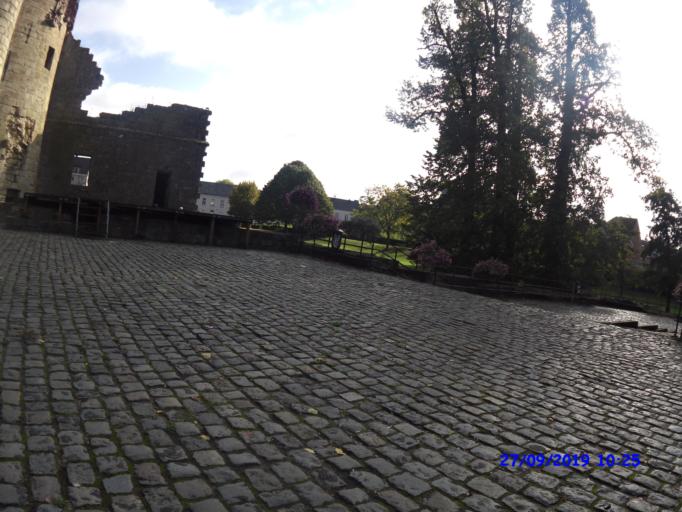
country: BE
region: Flanders
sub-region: Provincie Oost-Vlaanderen
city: Herzele
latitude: 50.8868
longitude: 3.8898
